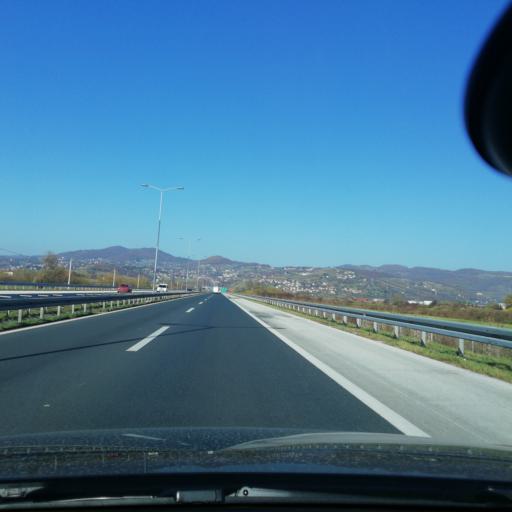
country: BA
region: Federation of Bosnia and Herzegovina
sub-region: Kanton Sarajevo
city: Sarajevo
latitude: 43.8606
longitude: 18.3067
